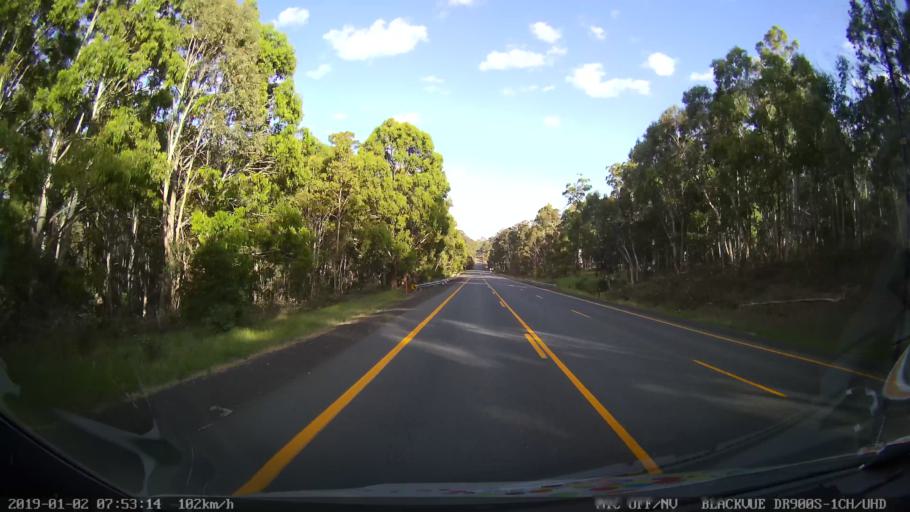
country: AU
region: New South Wales
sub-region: Tumut Shire
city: Tumut
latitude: -35.7077
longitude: 148.5089
